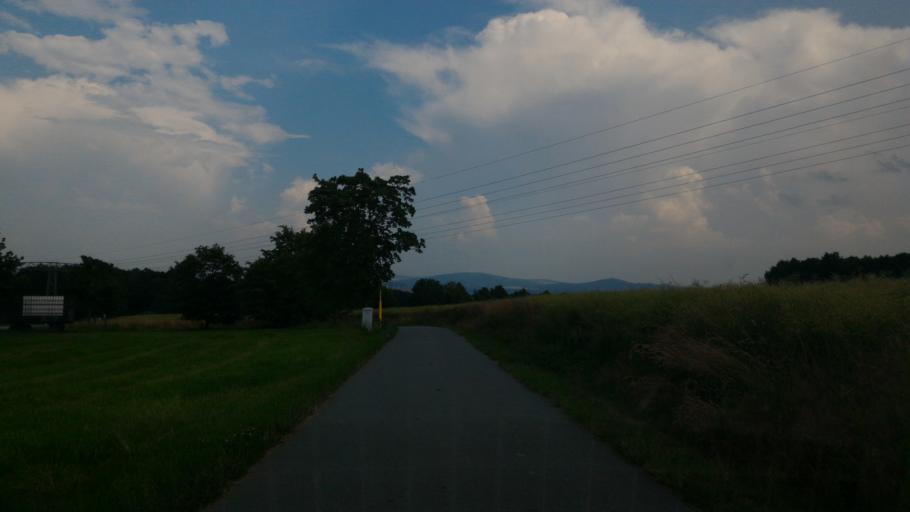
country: DE
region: Saxony
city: Hirschfelde
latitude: 50.9317
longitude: 14.8557
